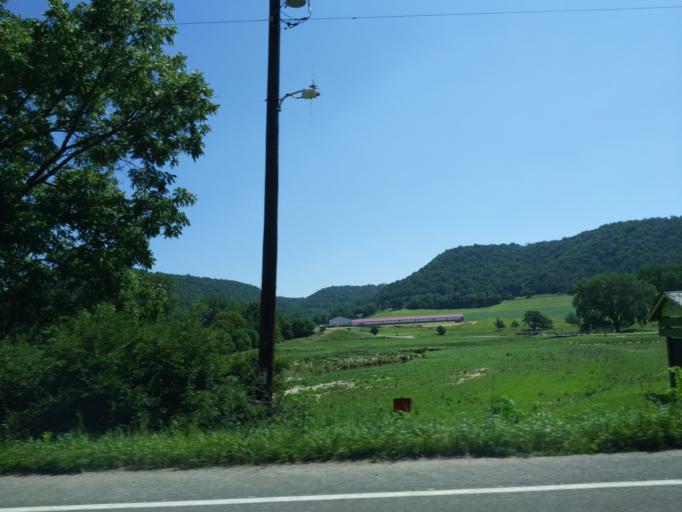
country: US
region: Wisconsin
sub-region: Vernon County
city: Westby
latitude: 43.6838
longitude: -91.0445
